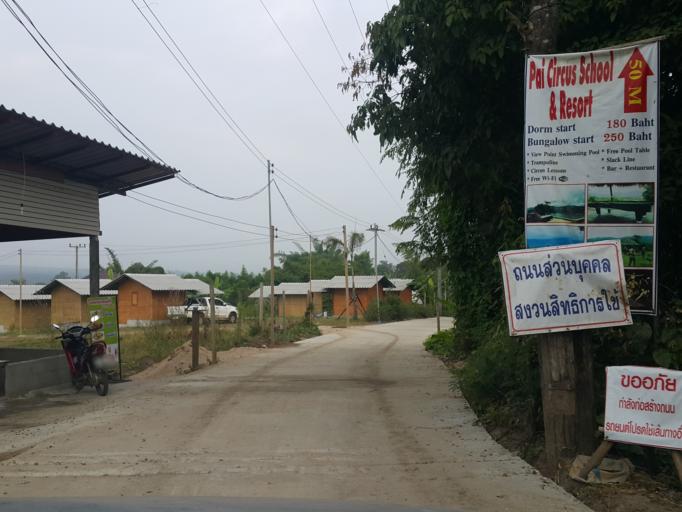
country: TH
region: Chiang Mai
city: Pai
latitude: 19.3616
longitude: 98.4495
